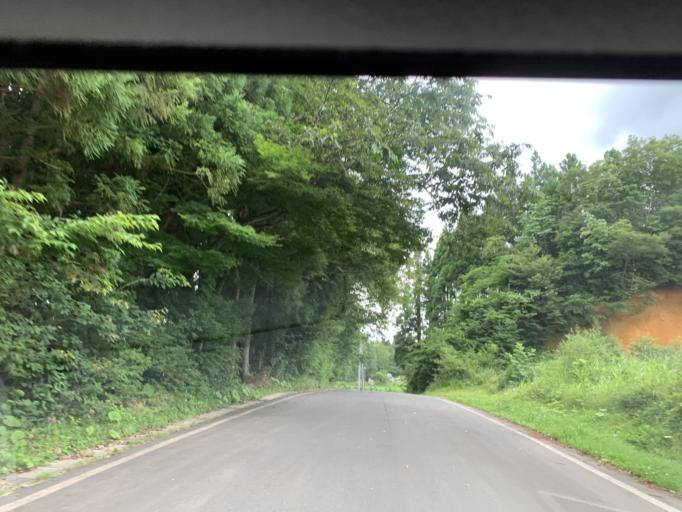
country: JP
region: Iwate
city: Ichinoseki
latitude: 38.9435
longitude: 141.0393
